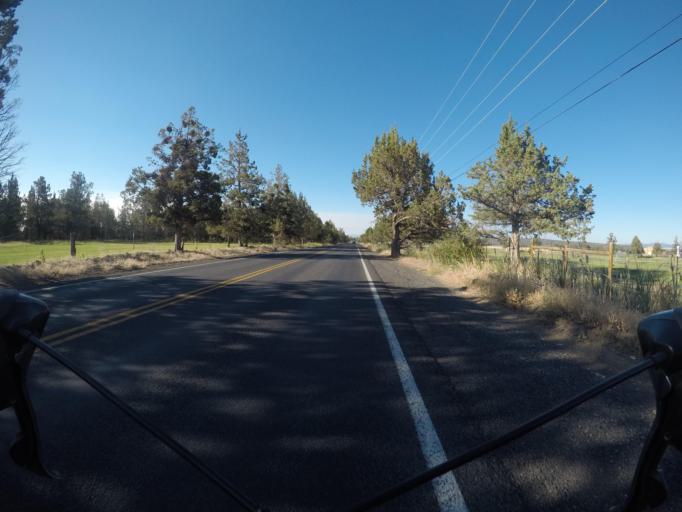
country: US
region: Oregon
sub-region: Deschutes County
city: Redmond
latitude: 44.2080
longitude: -121.2436
